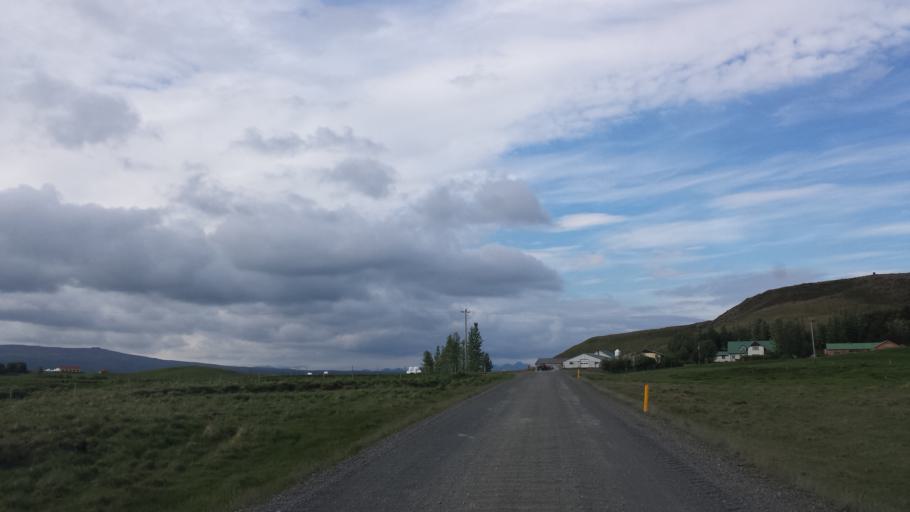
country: IS
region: South
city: Vestmannaeyjar
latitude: 64.2794
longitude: -20.2253
